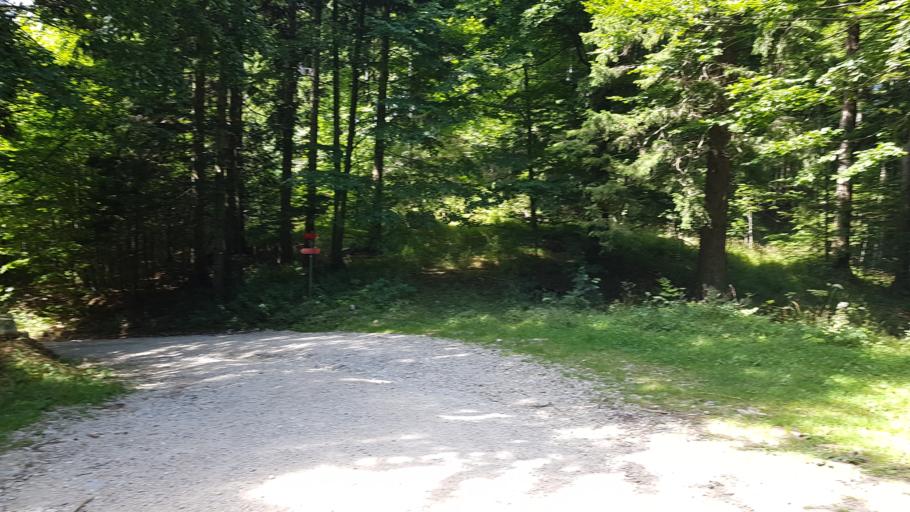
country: SI
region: Ajdovscina
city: Lokavec
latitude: 45.9750
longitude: 13.8515
